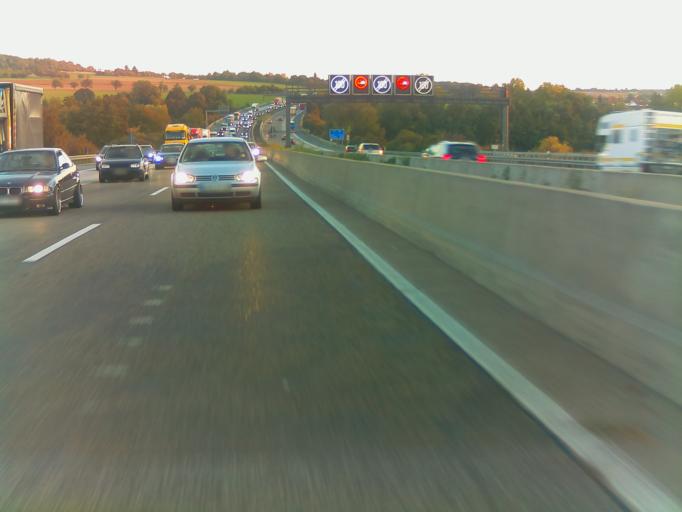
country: DE
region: Hesse
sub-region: Regierungsbezirk Darmstadt
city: Ober-Morlen
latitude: 50.3809
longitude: 8.7051
